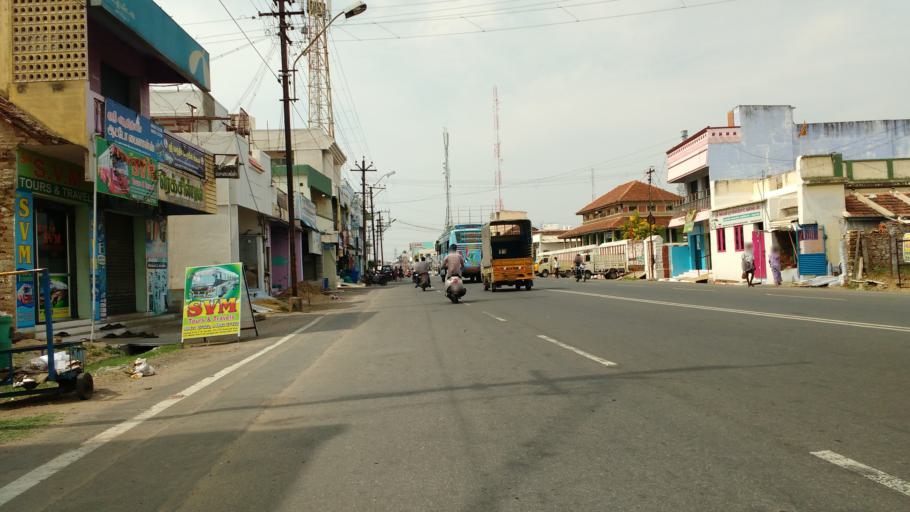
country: IN
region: Tamil Nadu
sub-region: Erode
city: Gobichettipalayam
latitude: 11.4548
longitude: 77.4411
